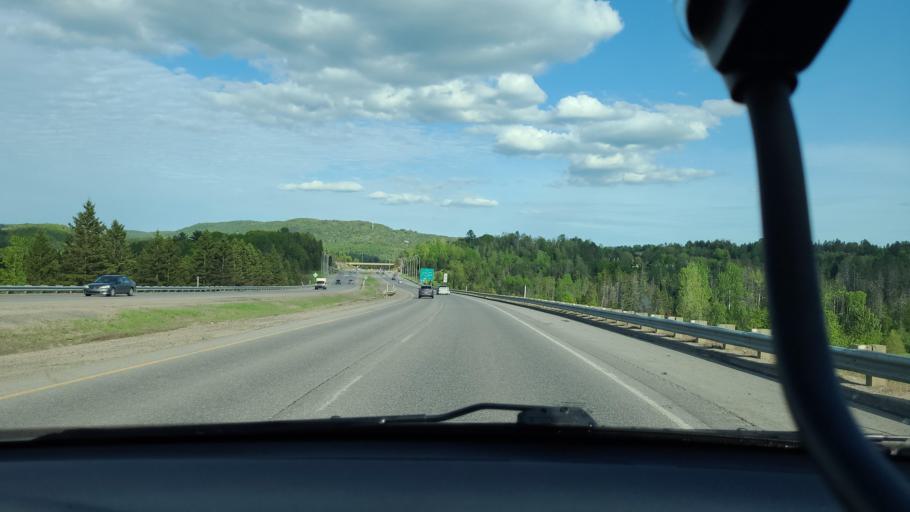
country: CA
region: Quebec
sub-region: Laurentides
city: Sainte-Adele
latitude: 45.9614
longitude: -74.1426
